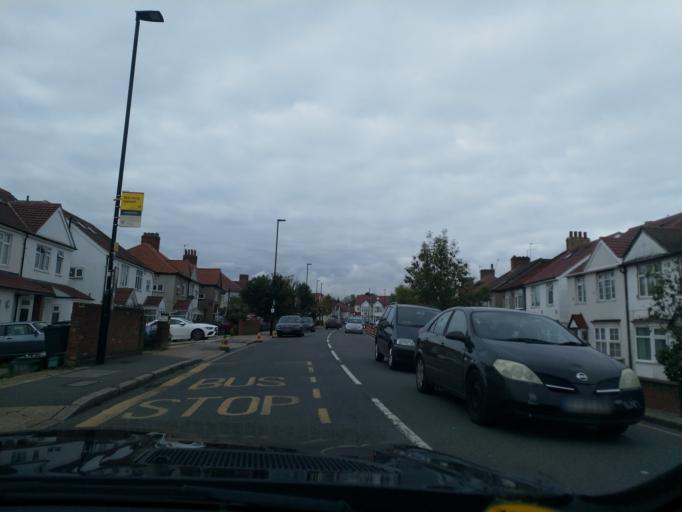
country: GB
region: England
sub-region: Greater London
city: Hounslow
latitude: 51.4758
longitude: -0.3601
